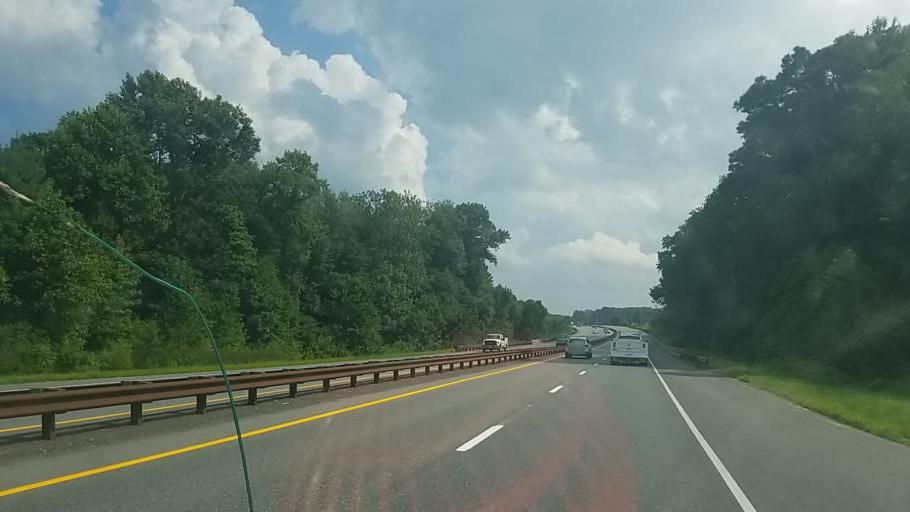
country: US
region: Delaware
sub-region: Sussex County
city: Selbyville
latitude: 38.4107
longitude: -75.2128
